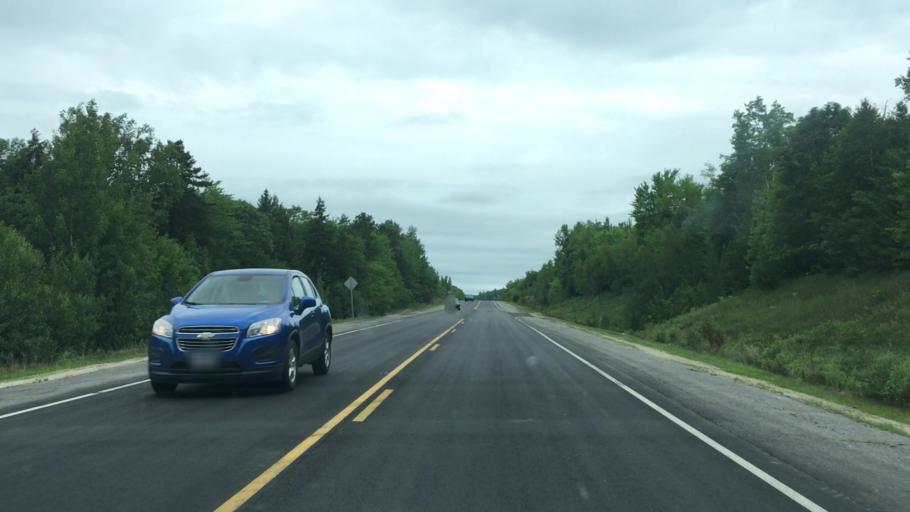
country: US
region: Maine
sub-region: Washington County
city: Cherryfield
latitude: 44.8855
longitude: -67.8569
